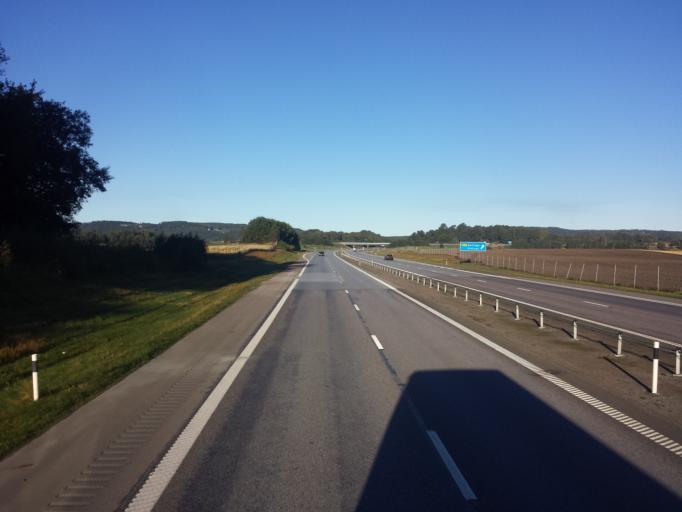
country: SE
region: Halland
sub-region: Halmstads Kommun
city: Getinge
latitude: 56.8048
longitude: 12.7491
